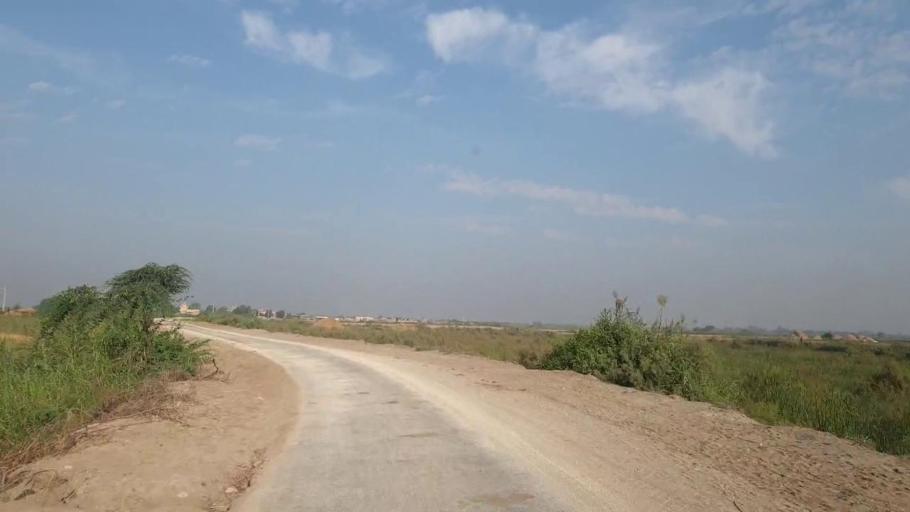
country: PK
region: Sindh
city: Tando Bago
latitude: 24.8535
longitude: 68.9690
